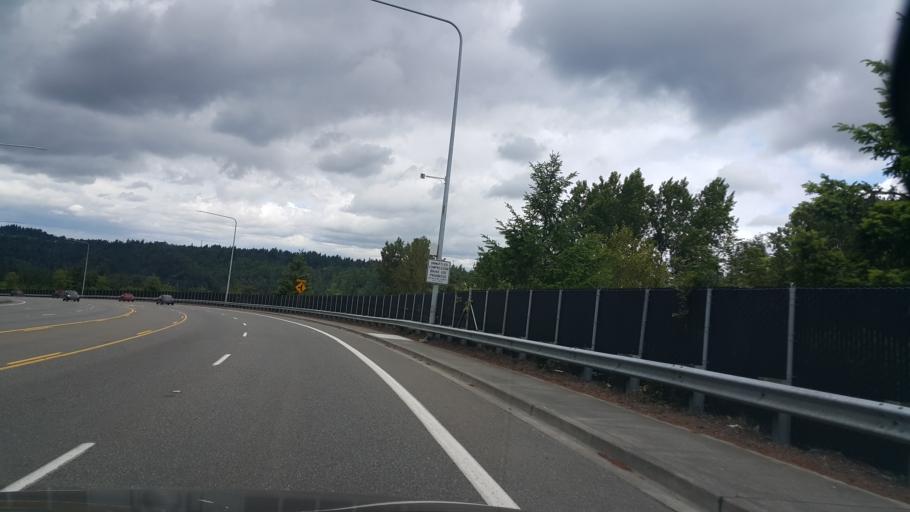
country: US
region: Washington
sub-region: King County
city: Fairwood
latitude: 47.4624
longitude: -122.1473
